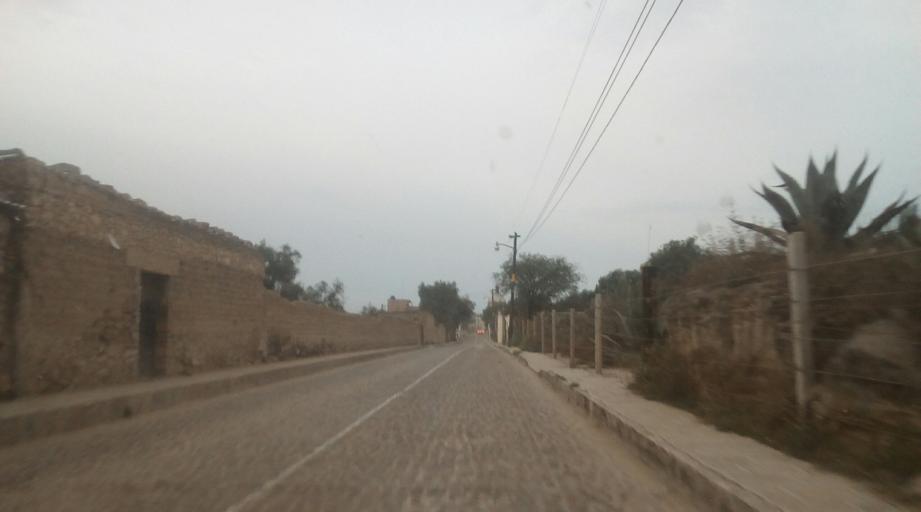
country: MX
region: Guanajuato
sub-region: San Luis de la Paz
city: San Ignacio
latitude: 21.2264
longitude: -100.4925
